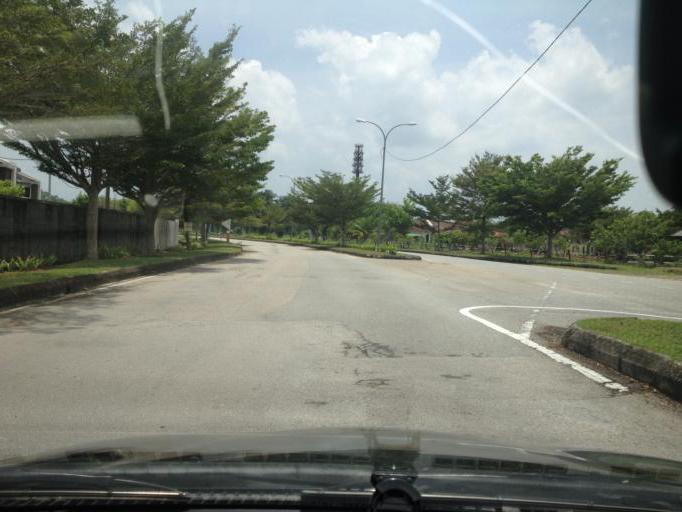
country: MY
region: Kedah
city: Sungai Petani
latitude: 5.6072
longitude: 100.5455
